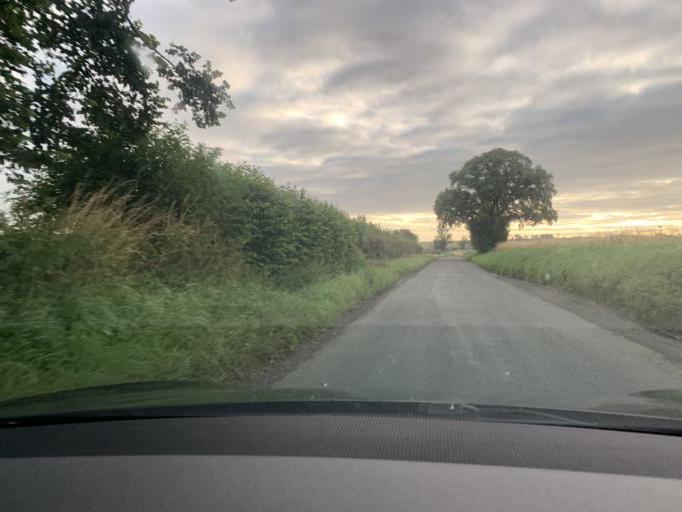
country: GB
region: England
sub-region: Wiltshire
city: Great Bedwyn
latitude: 51.3418
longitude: -1.6031
